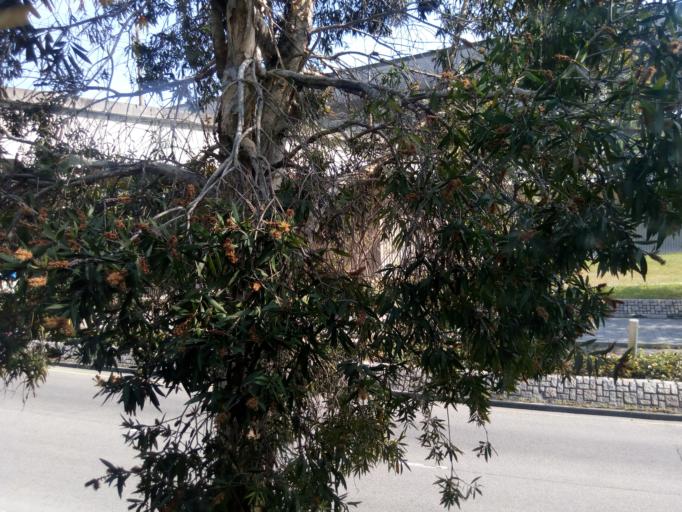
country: HK
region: Yuen Long
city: Yuen Long Kau Hui
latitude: 22.4508
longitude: 114.0069
